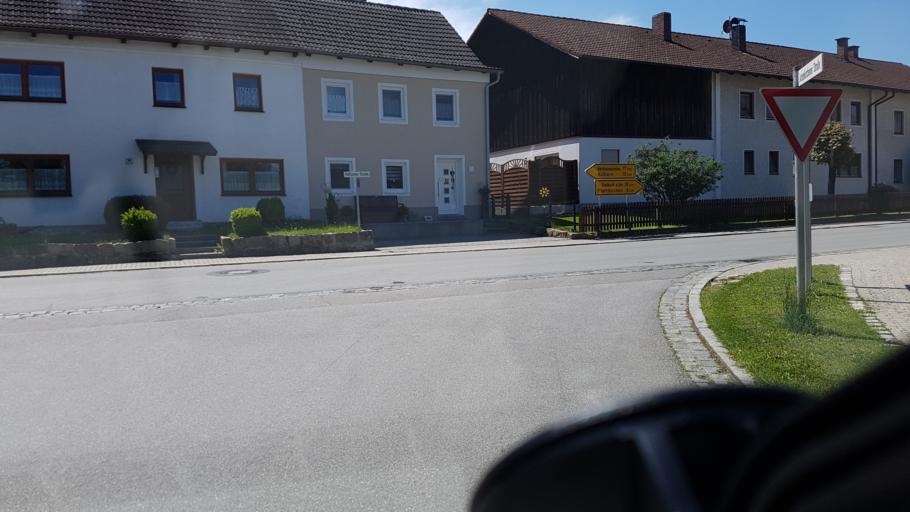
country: DE
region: Bavaria
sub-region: Lower Bavaria
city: Triftern
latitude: 48.3951
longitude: 13.0098
